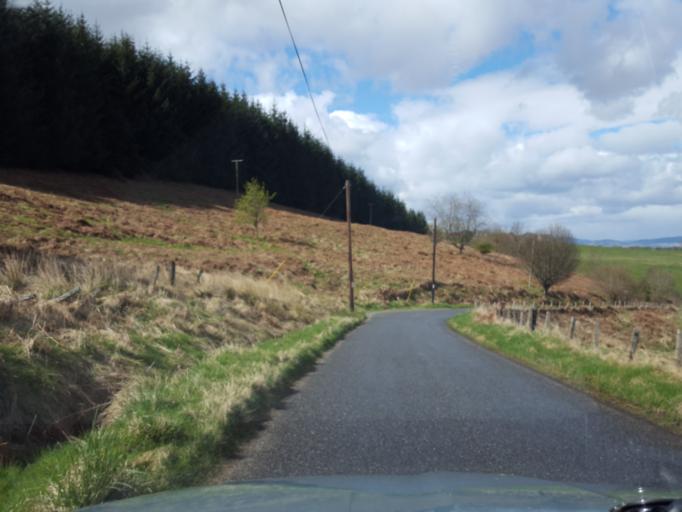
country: GB
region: Scotland
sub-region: Perth and Kinross
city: Auchterarder
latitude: 56.2818
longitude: -3.5773
